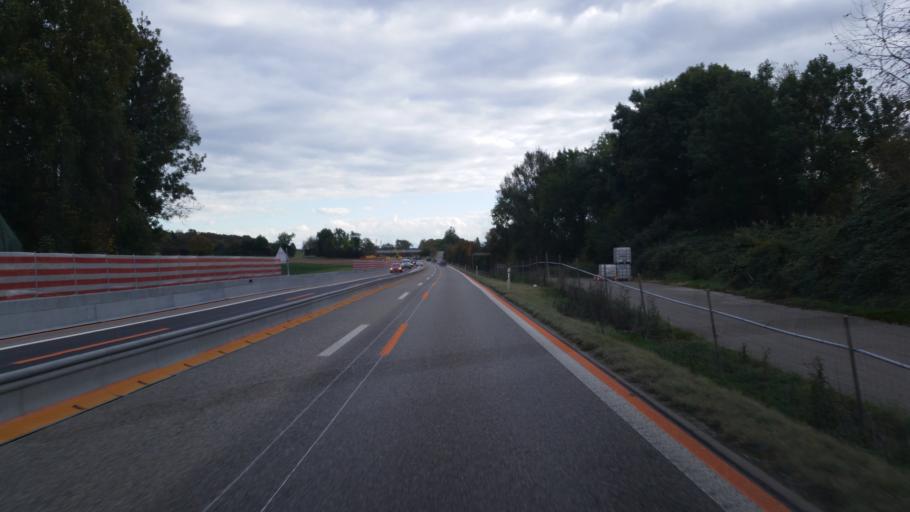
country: CH
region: Zurich
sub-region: Bezirk Buelach
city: Bachenbulach
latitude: 47.4790
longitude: 8.5509
